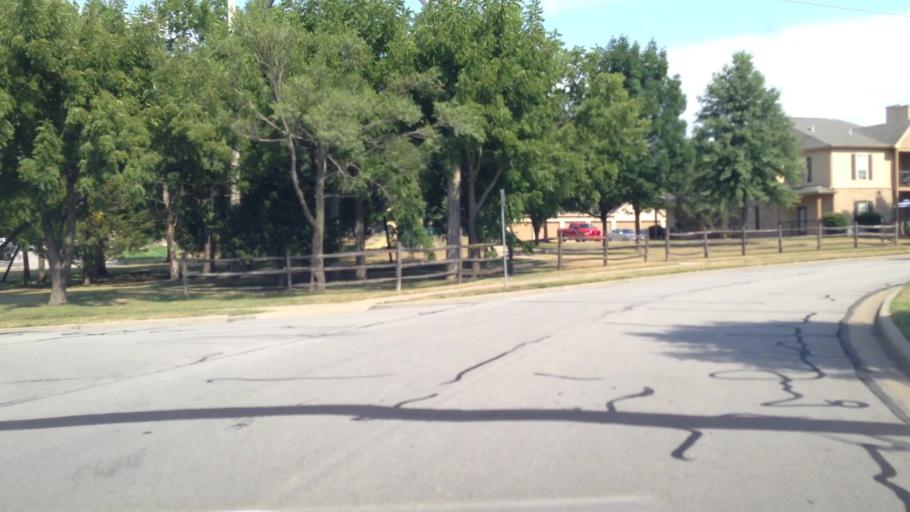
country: US
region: Kansas
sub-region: Johnson County
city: Lenexa
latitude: 38.9185
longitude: -94.7554
